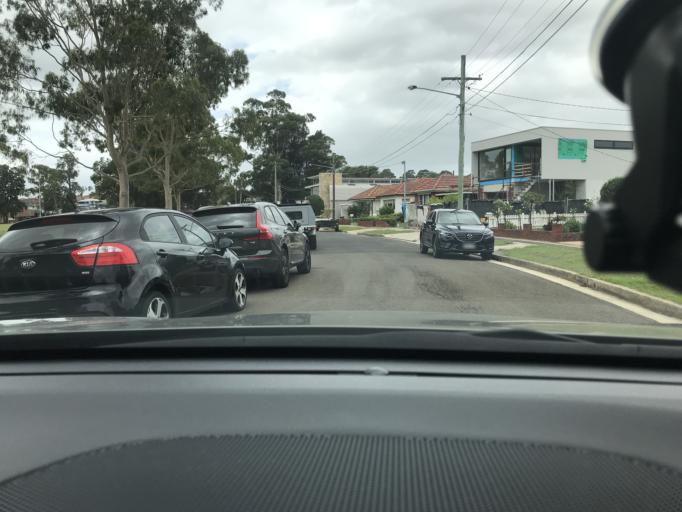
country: AU
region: New South Wales
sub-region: Canada Bay
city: Wareemba
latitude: -33.8627
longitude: 151.1276
